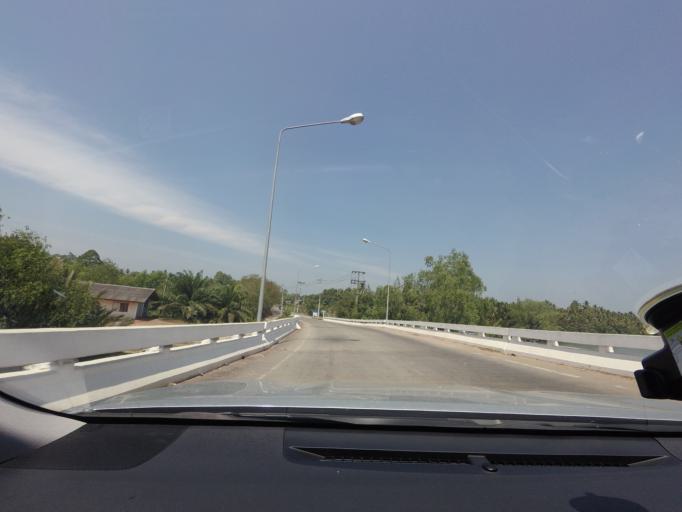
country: TH
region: Surat Thani
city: Phunphin
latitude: 9.1894
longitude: 99.2630
